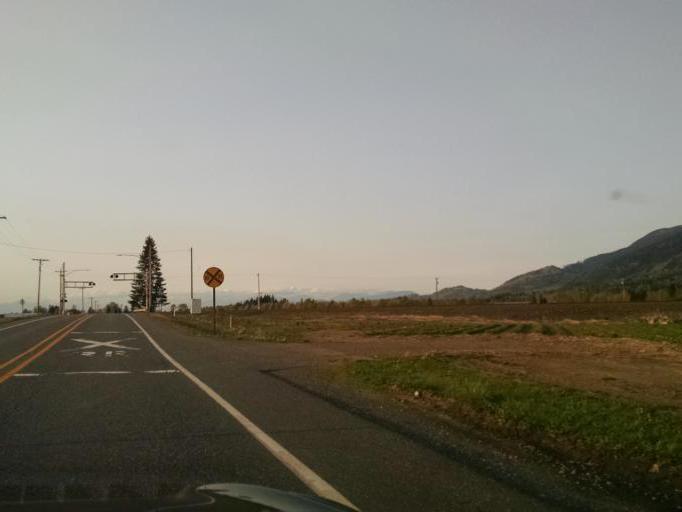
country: US
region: Washington
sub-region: Whatcom County
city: Nooksack
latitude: 48.8675
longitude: -122.3098
